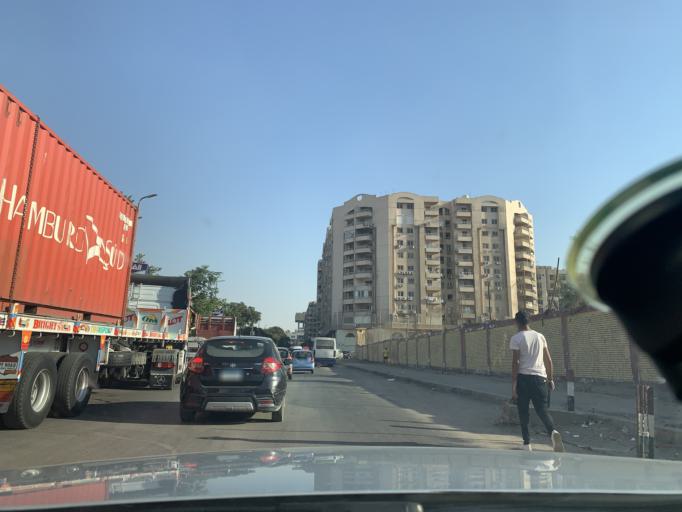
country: EG
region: Muhafazat al Qahirah
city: Cairo
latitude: 30.0395
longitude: 31.3461
